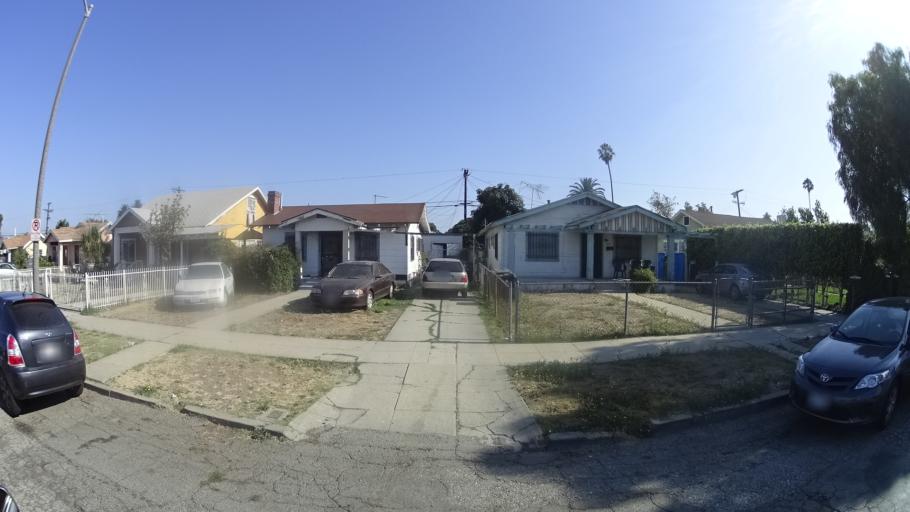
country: US
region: California
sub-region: Los Angeles County
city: Westmont
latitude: 33.9762
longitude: -118.3037
